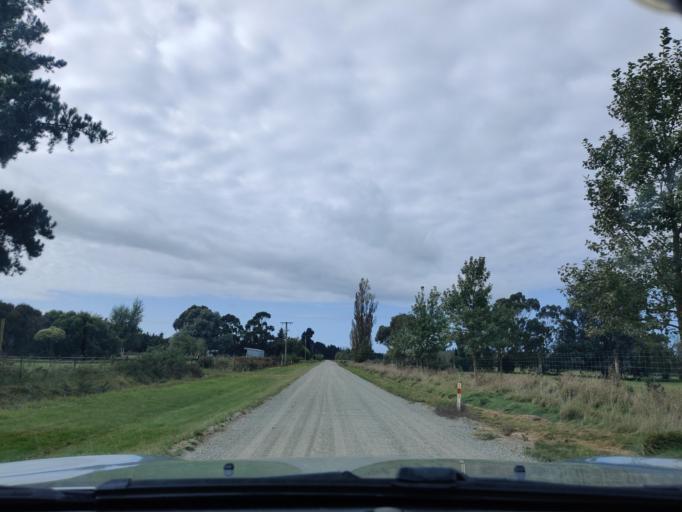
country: NZ
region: Canterbury
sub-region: Hurunui District
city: Amberley
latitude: -43.2275
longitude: 172.7101
